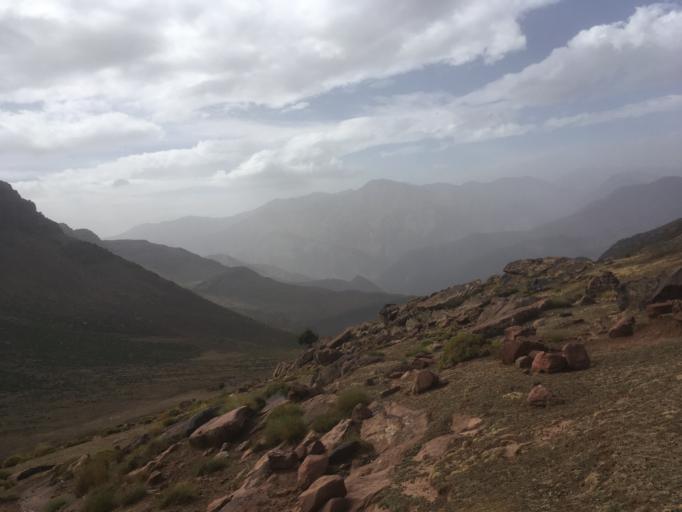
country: MA
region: Marrakech-Tensift-Al Haouz
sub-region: Al-Haouz
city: Tidili Mesfioua
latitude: 31.3238
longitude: -7.6702
